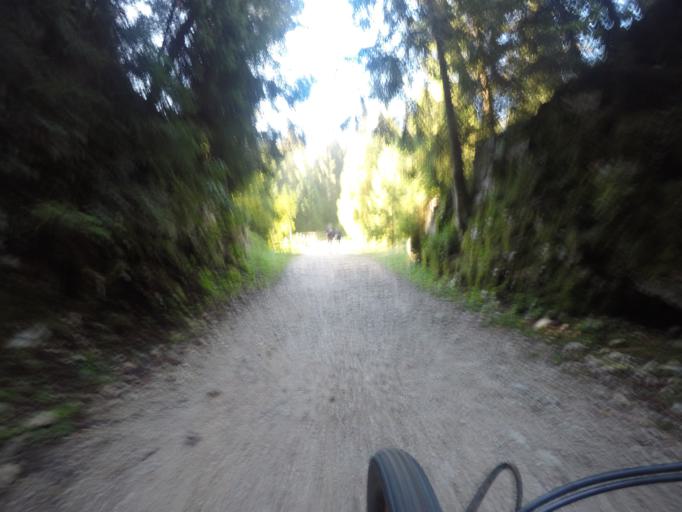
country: IT
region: Veneto
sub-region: Provincia di Vicenza
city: Canove di Roana
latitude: 45.8491
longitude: 11.4738
